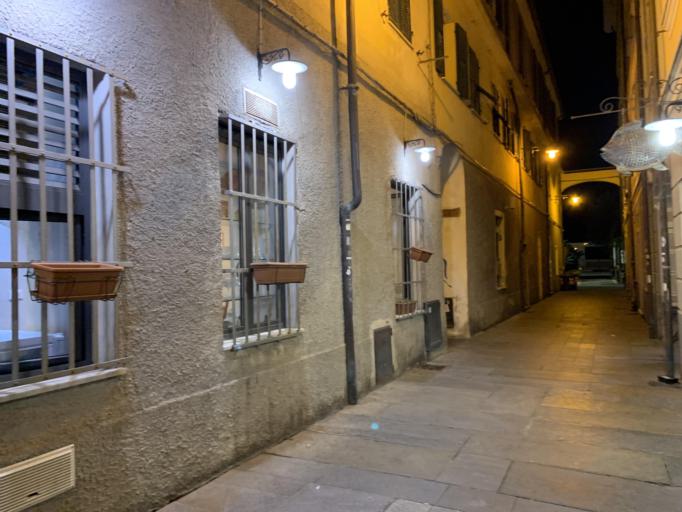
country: IT
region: Liguria
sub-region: Provincia di Savona
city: Finale Ligure
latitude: 44.1689
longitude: 8.3436
